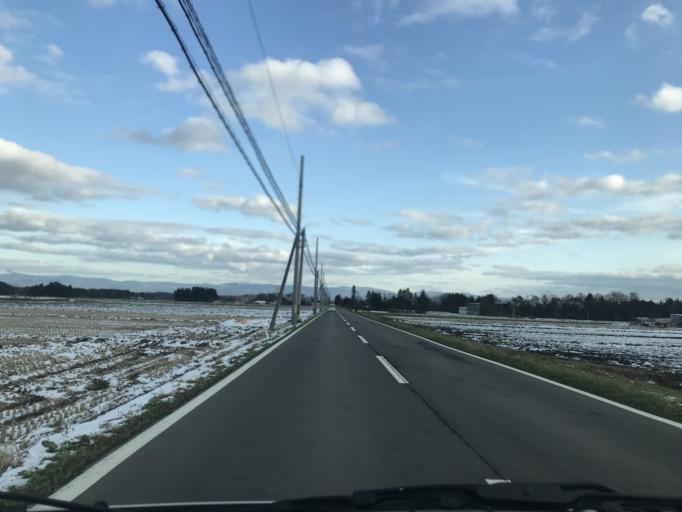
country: JP
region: Iwate
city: Kitakami
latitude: 39.2089
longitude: 141.0386
